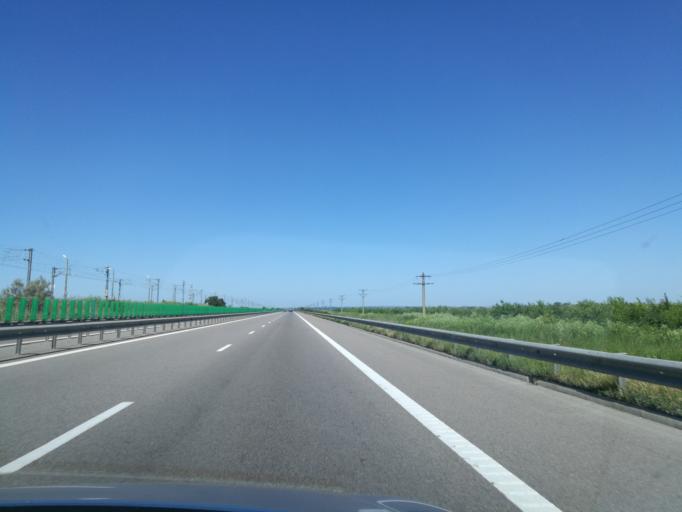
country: RO
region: Constanta
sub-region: Oras Cernavoda
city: Cernavoda
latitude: 44.3547
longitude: 27.9608
